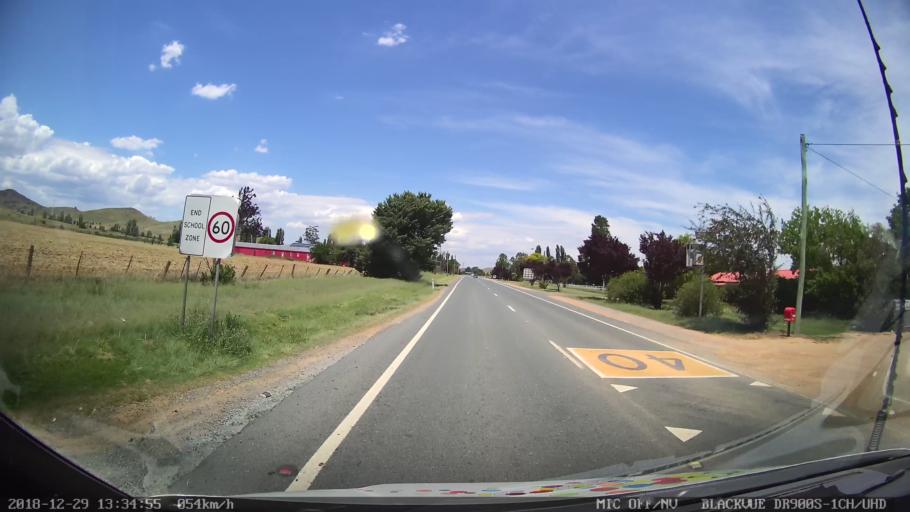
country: AU
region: New South Wales
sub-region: Cooma-Monaro
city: Cooma
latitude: -35.9563
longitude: 149.1487
